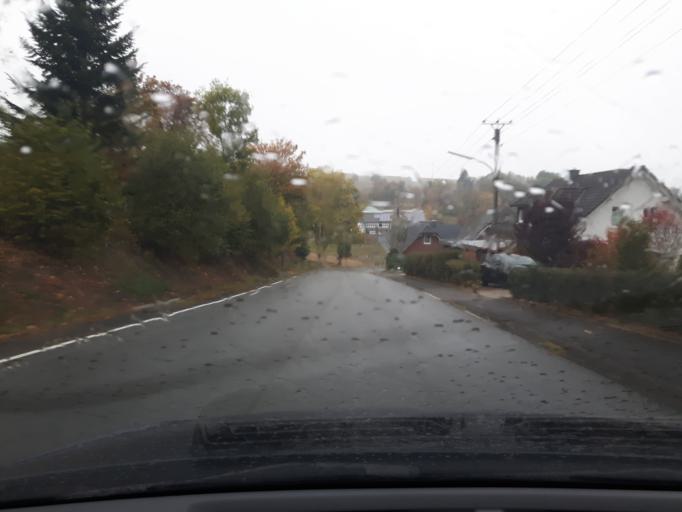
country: DE
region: North Rhine-Westphalia
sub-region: Regierungsbezirk Arnsberg
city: Bad Berleburg
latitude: 50.9903
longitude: 8.3923
